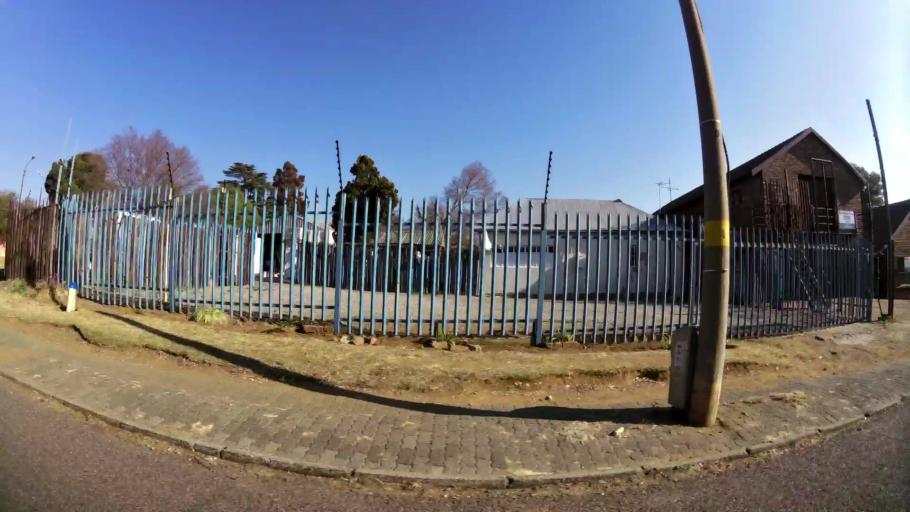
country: ZA
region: Gauteng
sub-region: City of Johannesburg Metropolitan Municipality
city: Modderfontein
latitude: -26.1365
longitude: 28.1604
